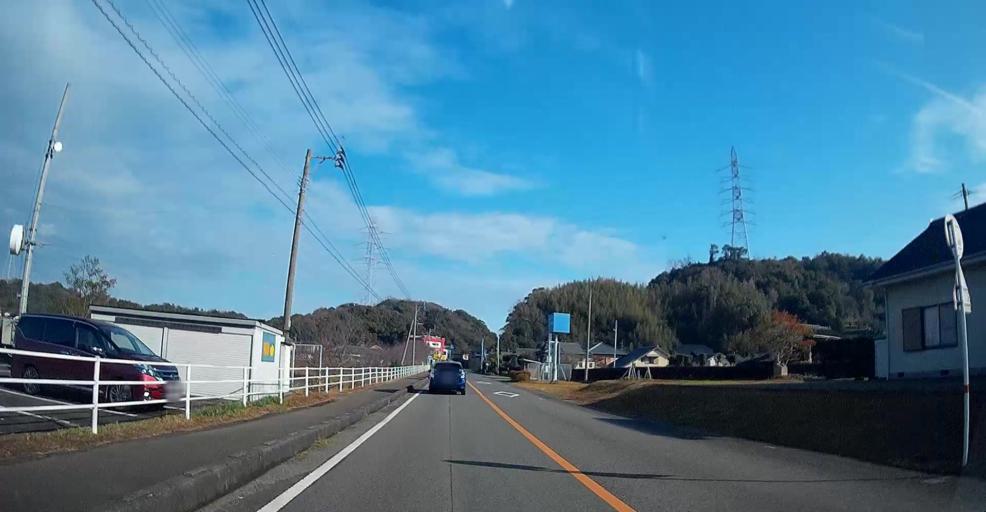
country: JP
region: Kumamoto
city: Yatsushiro
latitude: 32.5184
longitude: 130.4514
